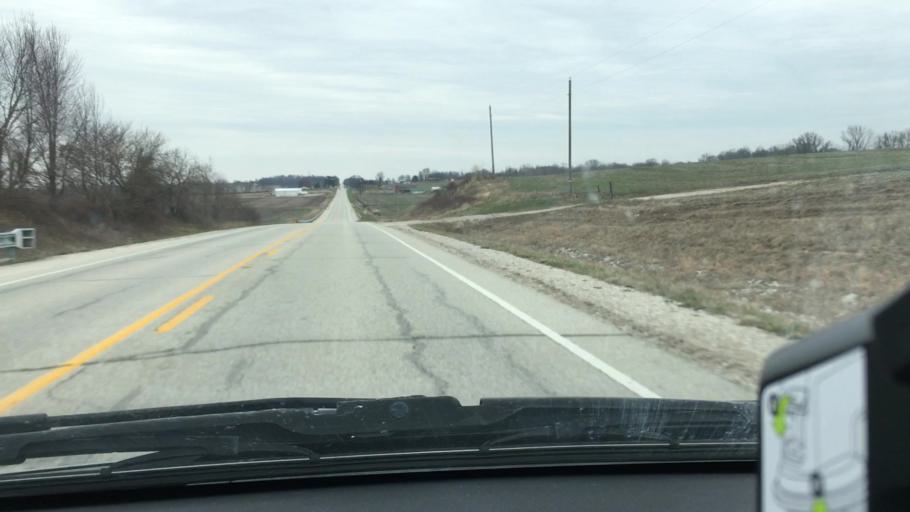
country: US
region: Indiana
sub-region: Greene County
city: Bloomfield
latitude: 38.9668
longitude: -87.0169
